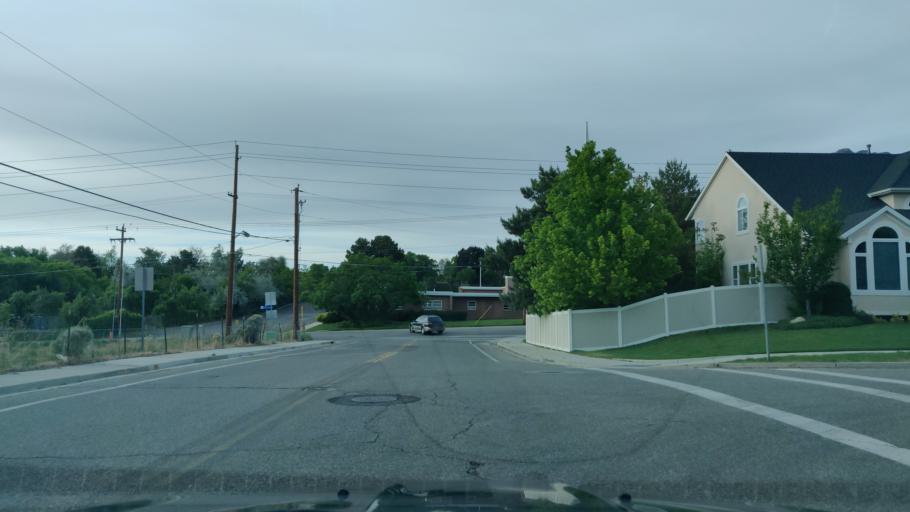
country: US
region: Utah
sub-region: Salt Lake County
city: Cottonwood Heights
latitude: 40.6088
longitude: -111.8102
